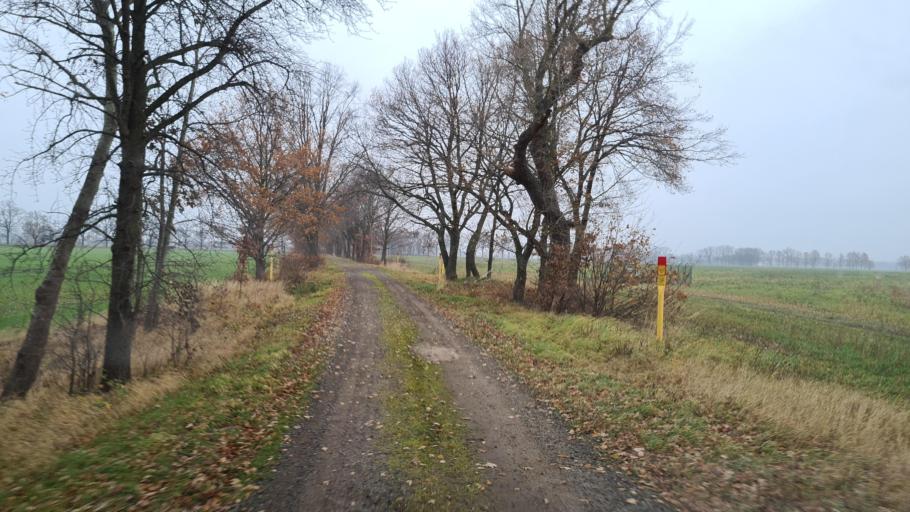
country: DE
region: Brandenburg
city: Schraden
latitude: 51.4141
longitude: 13.7043
